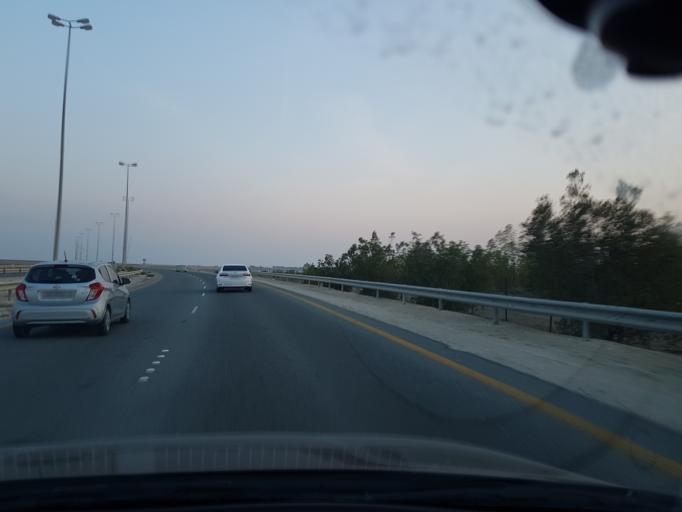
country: BH
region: Central Governorate
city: Dar Kulayb
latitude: 26.0121
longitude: 50.4835
